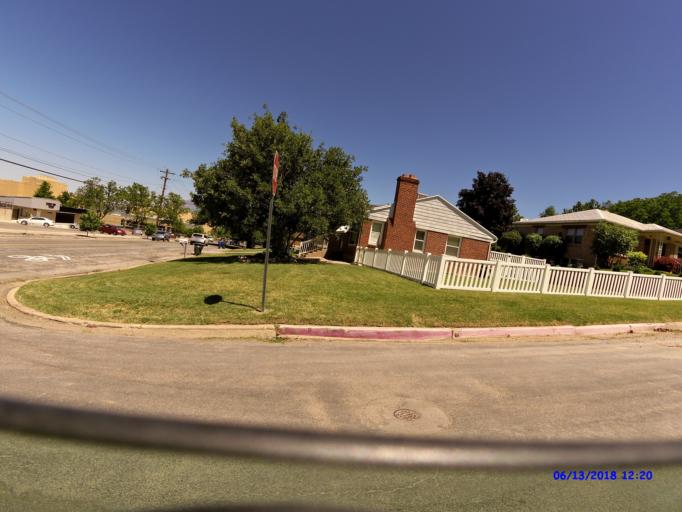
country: US
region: Utah
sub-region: Weber County
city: Ogden
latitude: 41.2110
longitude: -111.9456
